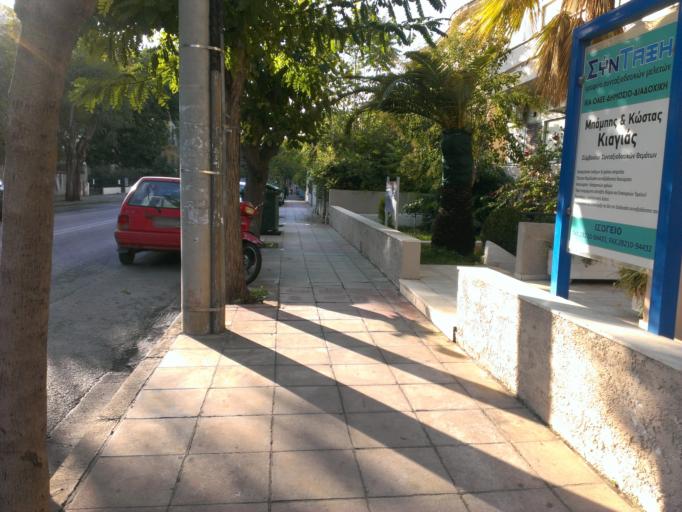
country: GR
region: Crete
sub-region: Nomos Chanias
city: Chania
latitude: 35.5103
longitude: 24.0278
